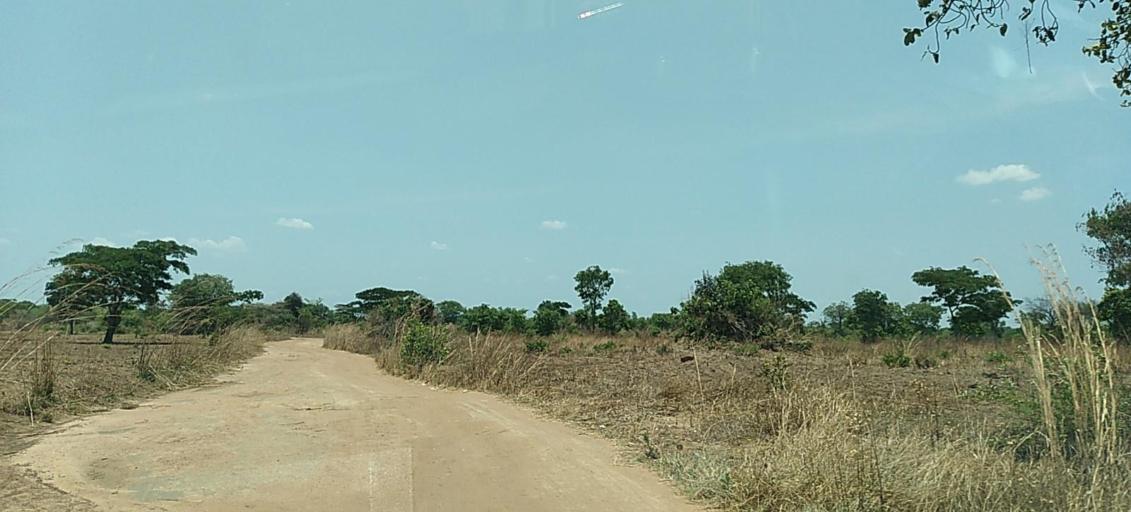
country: ZM
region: Copperbelt
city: Luanshya
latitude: -13.0946
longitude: 28.4064
